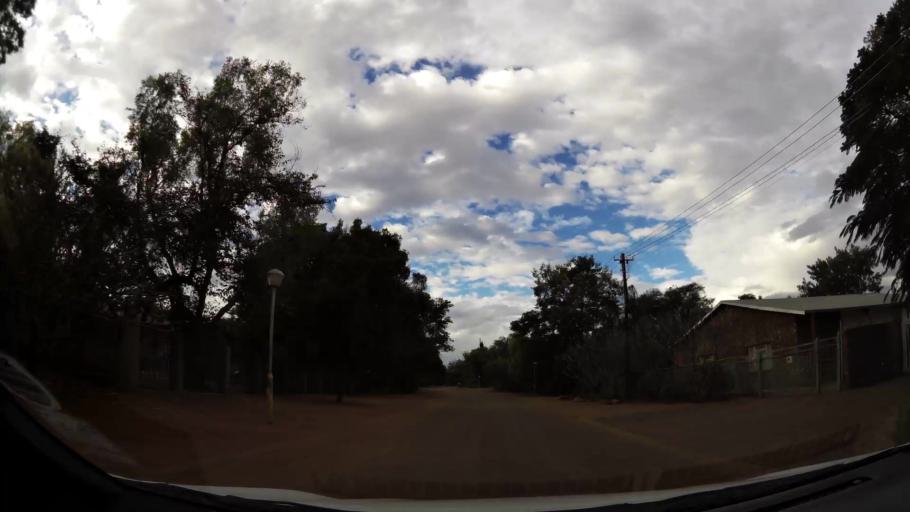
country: ZA
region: Limpopo
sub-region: Waterberg District Municipality
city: Modimolle
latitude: -24.5133
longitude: 28.7104
